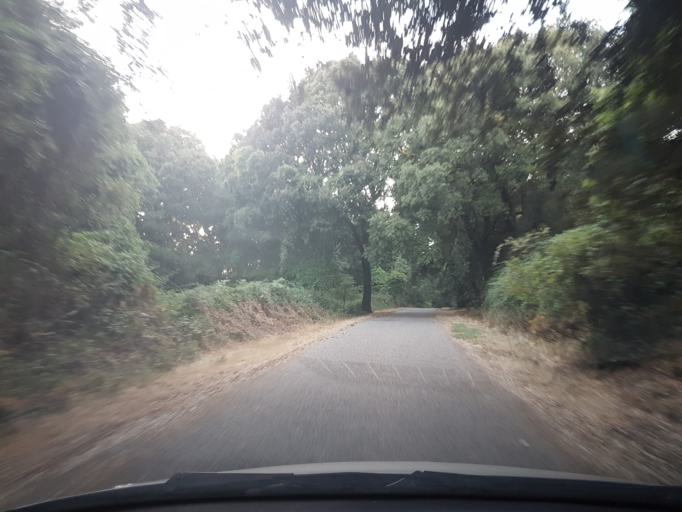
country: IT
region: Sardinia
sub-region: Provincia di Oristano
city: Seneghe
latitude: 40.1131
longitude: 8.5823
